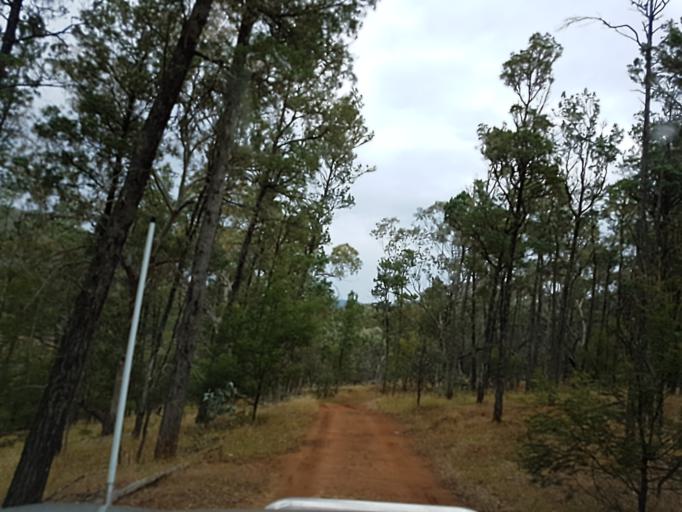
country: AU
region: New South Wales
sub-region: Snowy River
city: Jindabyne
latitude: -36.9352
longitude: 148.4001
